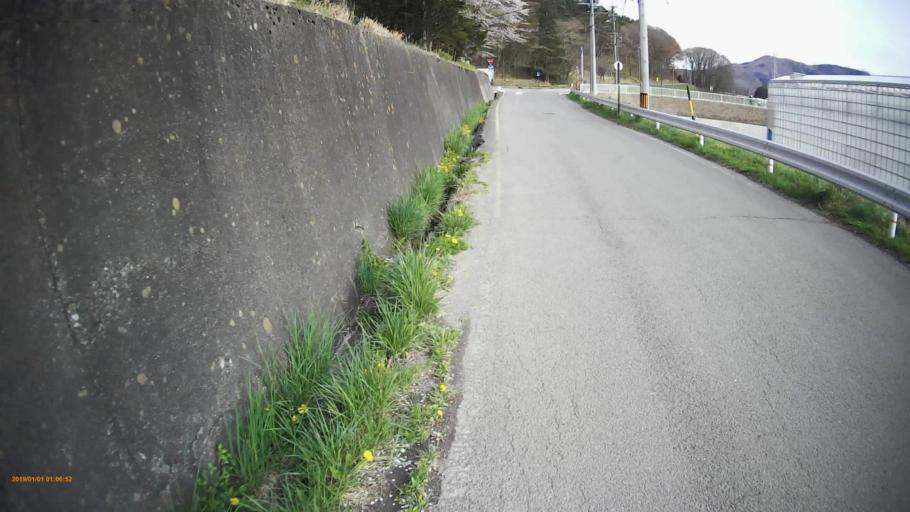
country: JP
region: Nagano
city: Chino
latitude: 35.9165
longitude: 138.2188
